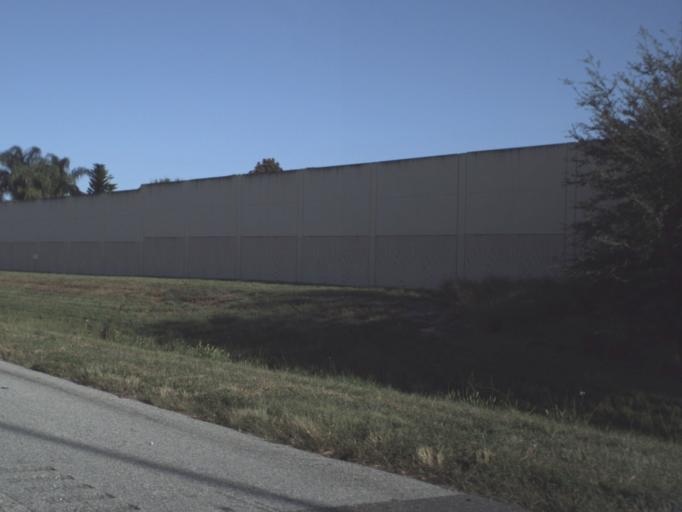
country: US
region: Florida
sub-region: Orange County
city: Gotha
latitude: 28.5165
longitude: -81.4999
